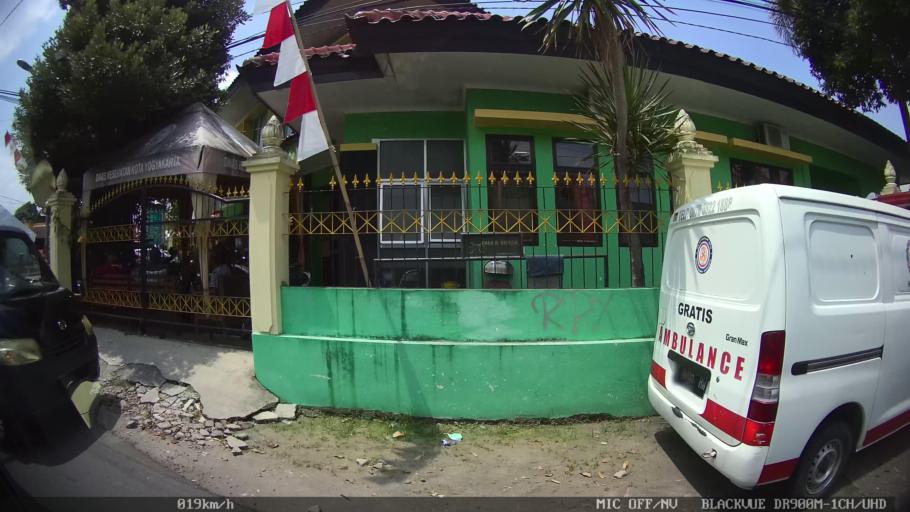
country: ID
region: Daerah Istimewa Yogyakarta
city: Yogyakarta
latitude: -7.8138
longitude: 110.3948
